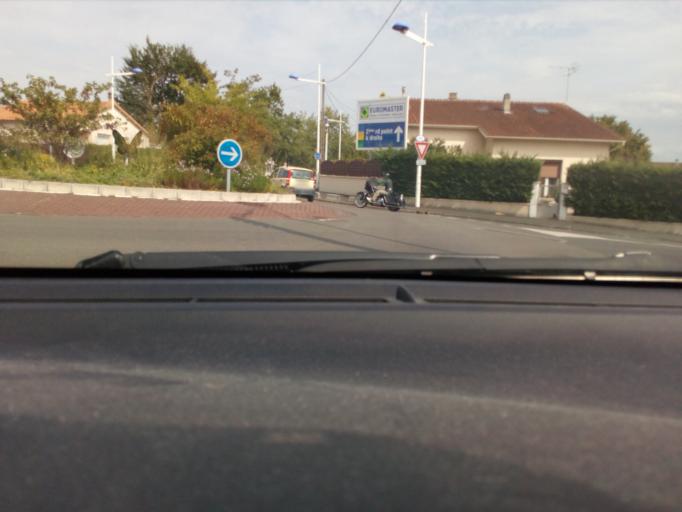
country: FR
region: Poitou-Charentes
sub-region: Departement de la Charente
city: Angouleme
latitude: 45.6643
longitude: 0.1478
